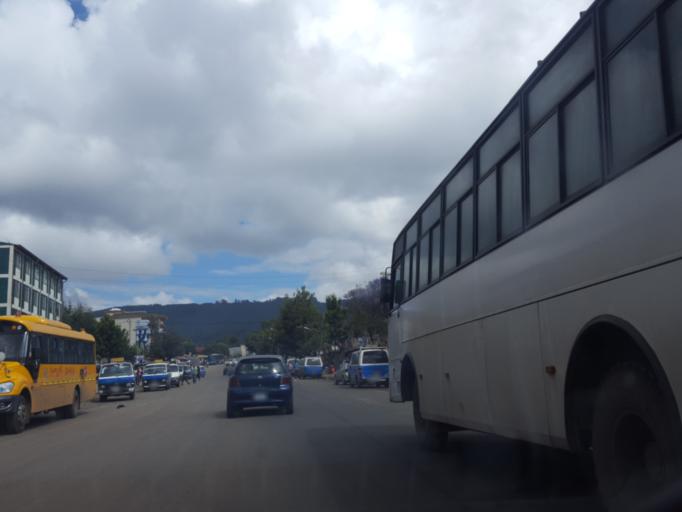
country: ET
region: Adis Abeba
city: Addis Ababa
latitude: 9.0603
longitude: 38.7620
